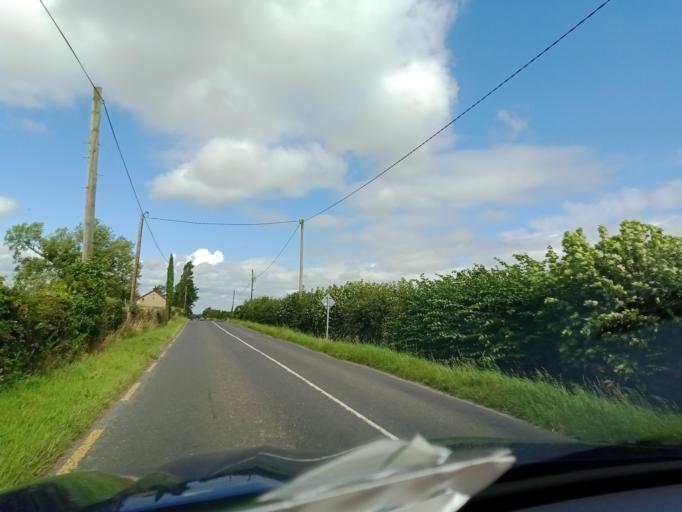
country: IE
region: Leinster
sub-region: Laois
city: Portlaoise
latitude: 52.9670
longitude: -7.2957
